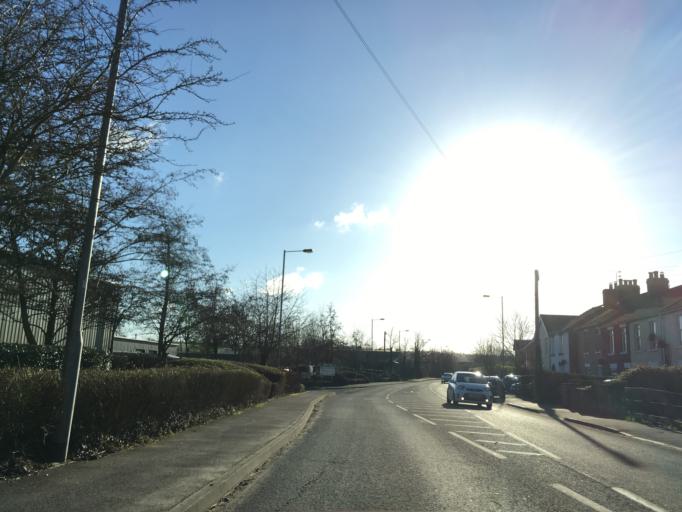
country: GB
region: England
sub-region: Borough of Swindon
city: Wroughton
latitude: 51.5331
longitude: -1.7850
